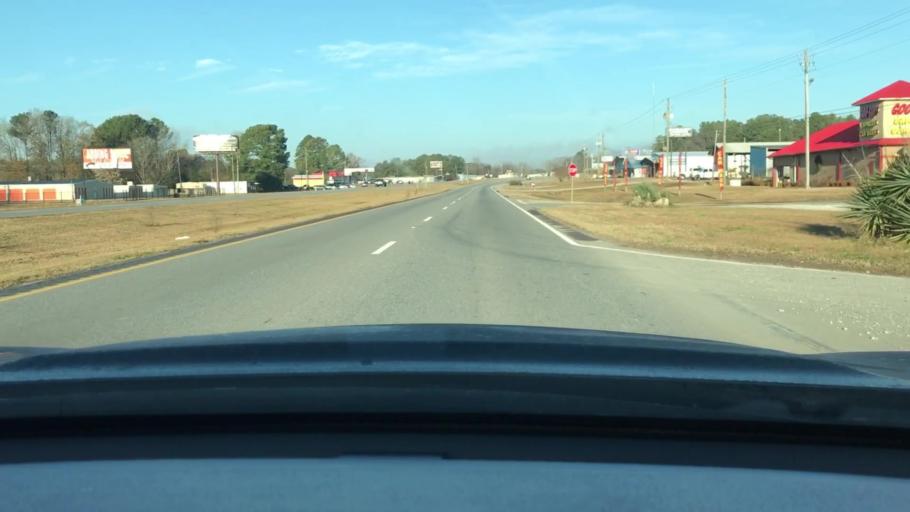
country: US
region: Alabama
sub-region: Talladega County
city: Mignon
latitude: 33.1776
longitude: -86.2939
